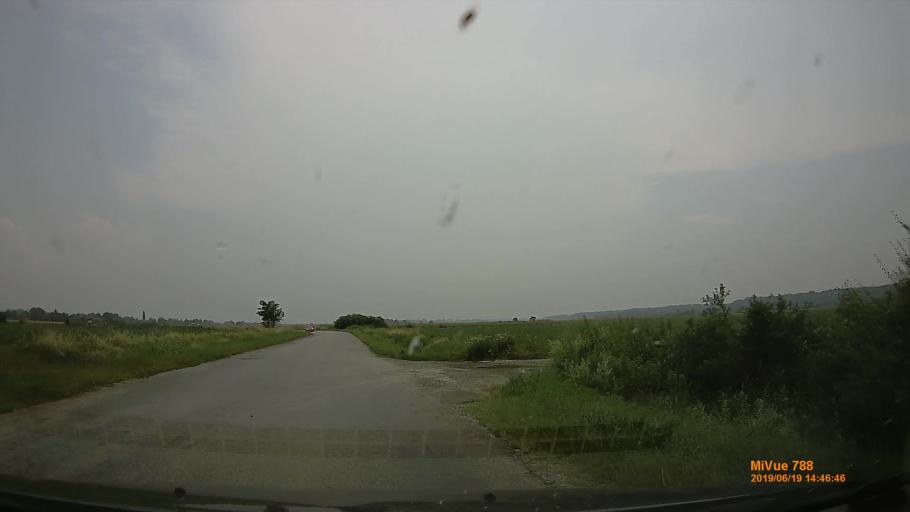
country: HU
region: Baranya
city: Szigetvar
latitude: 46.0023
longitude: 17.8256
